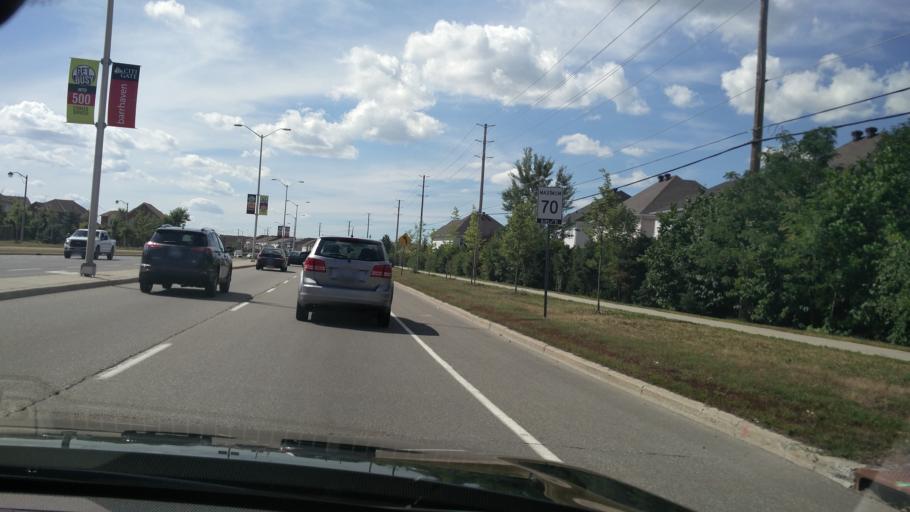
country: CA
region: Ontario
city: Bells Corners
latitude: 45.2754
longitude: -75.7265
